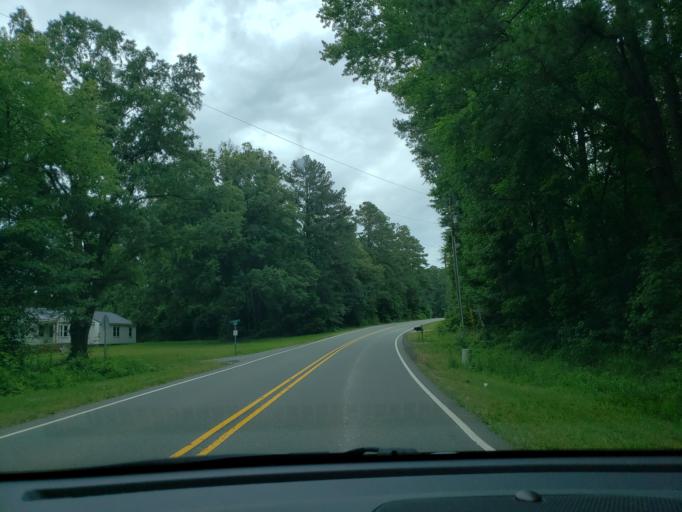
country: US
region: North Carolina
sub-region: Chatham County
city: Fearrington Village
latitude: 35.7660
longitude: -79.0065
